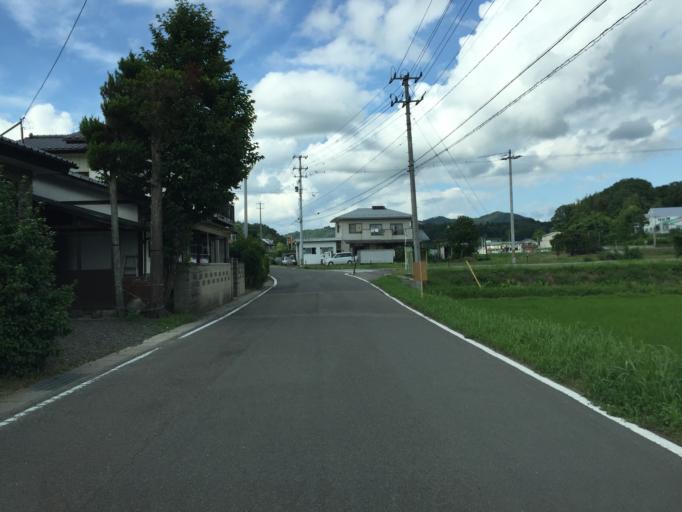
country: JP
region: Fukushima
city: Fukushima-shi
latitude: 37.6713
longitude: 140.5561
